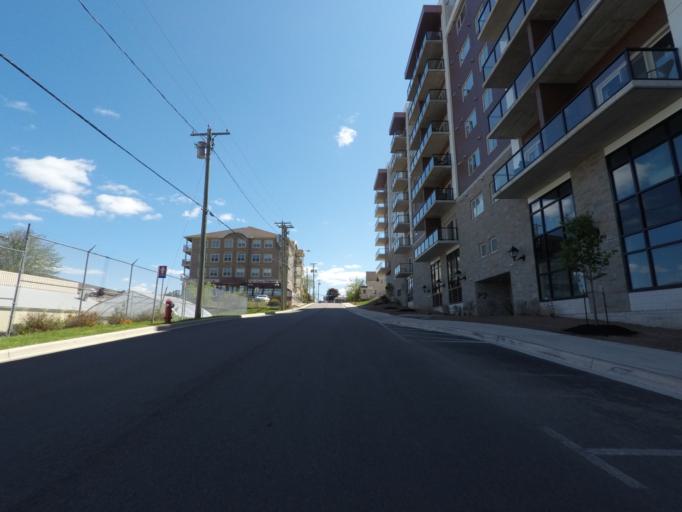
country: CA
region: New Brunswick
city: Moncton
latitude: 46.0967
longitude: -64.7557
